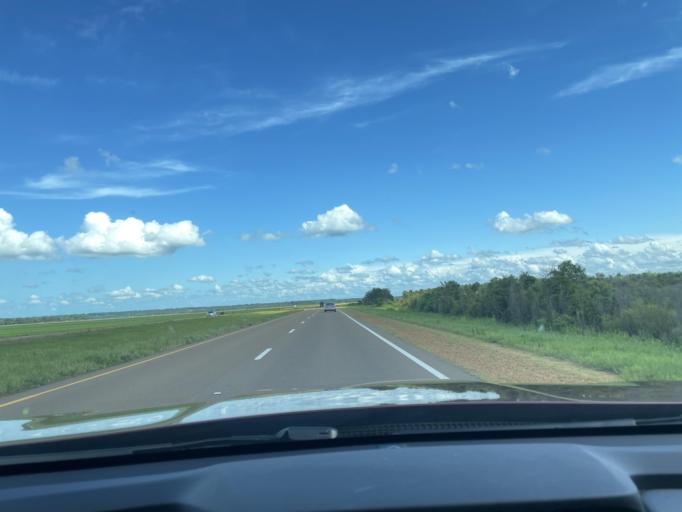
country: US
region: Mississippi
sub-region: Yazoo County
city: Yazoo City
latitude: 32.9539
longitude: -90.4255
